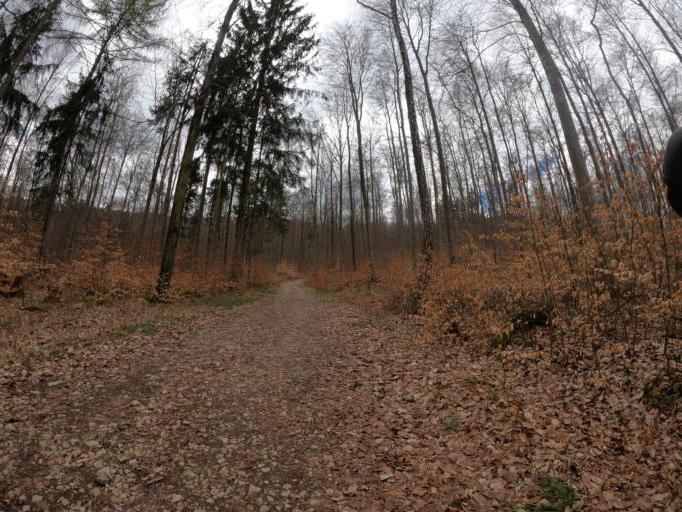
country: DE
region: Baden-Wuerttemberg
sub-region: Tuebingen Region
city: Mossingen
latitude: 48.3790
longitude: 9.0493
